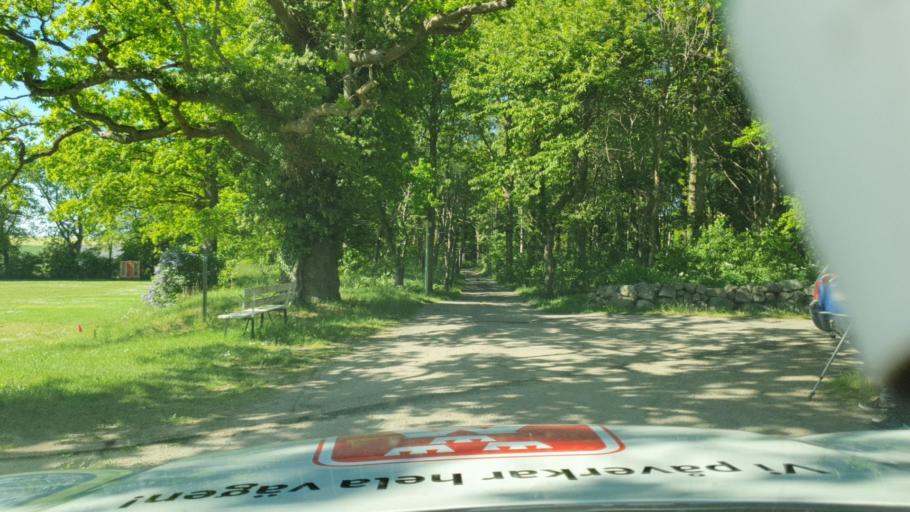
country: SE
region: Skane
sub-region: Simrishamns Kommun
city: Simrishamn
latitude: 55.4928
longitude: 14.2742
